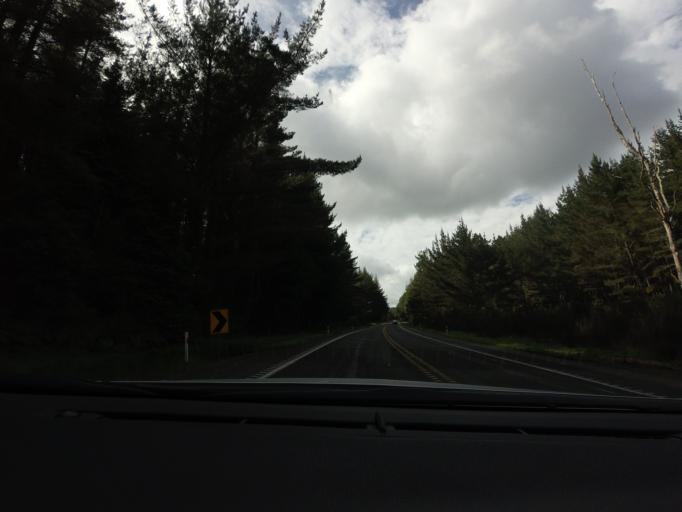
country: NZ
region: Bay of Plenty
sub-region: Rotorua District
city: Rotorua
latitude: -38.1857
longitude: 176.2562
